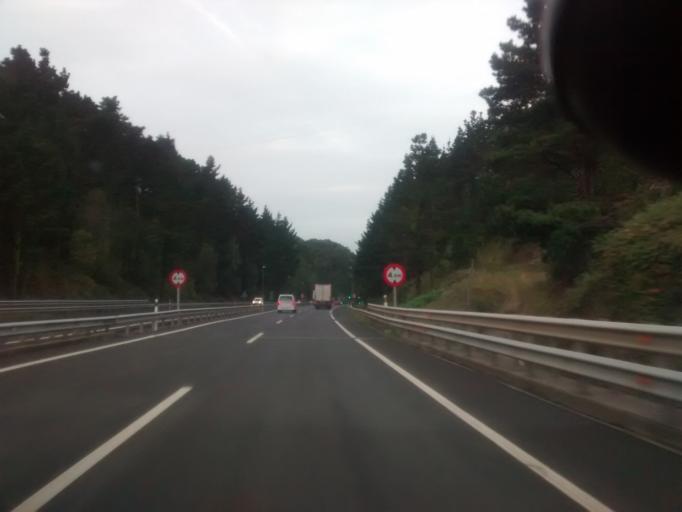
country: ES
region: Basque Country
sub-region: Provincia de Guipuzcoa
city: Deba
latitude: 43.2819
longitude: -2.3593
